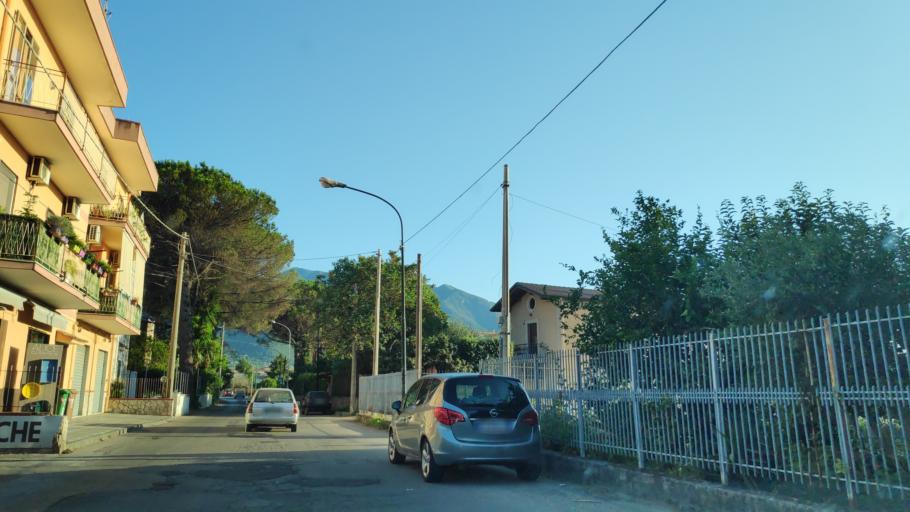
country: IT
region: Campania
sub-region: Provincia di Salerno
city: Pagani
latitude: 40.7525
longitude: 14.6146
